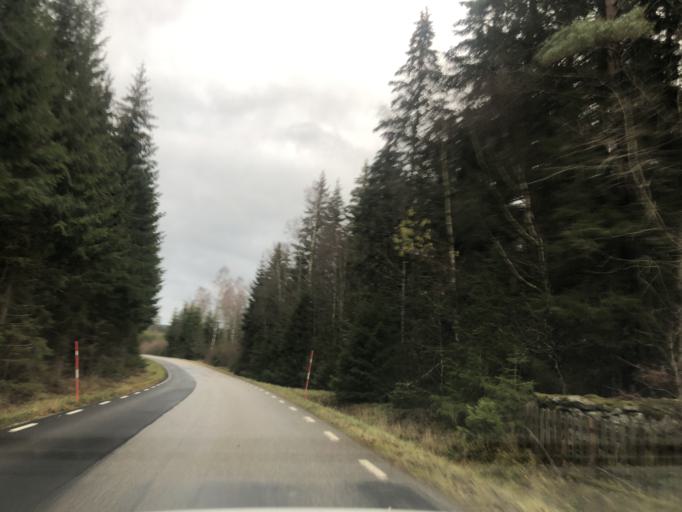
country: SE
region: Vaestra Goetaland
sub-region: Boras Kommun
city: Dalsjofors
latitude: 57.8133
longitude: 13.1991
